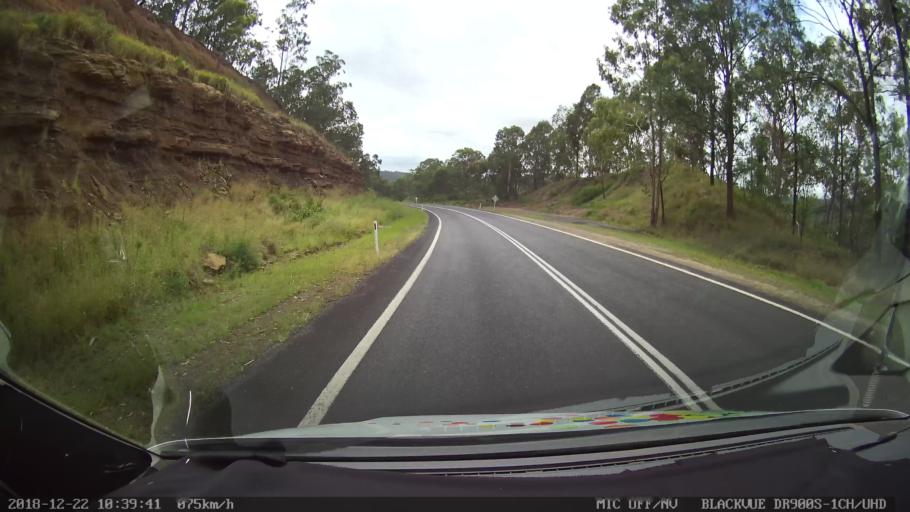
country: AU
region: New South Wales
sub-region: Clarence Valley
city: South Grafton
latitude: -29.6304
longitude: 152.7372
